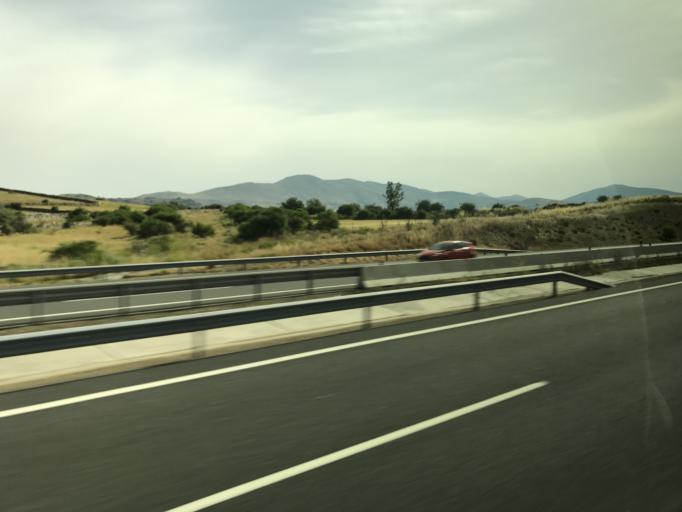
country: ES
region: Castille and Leon
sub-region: Provincia de Segovia
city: Vegas de Matute
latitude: 40.7392
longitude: -4.2393
